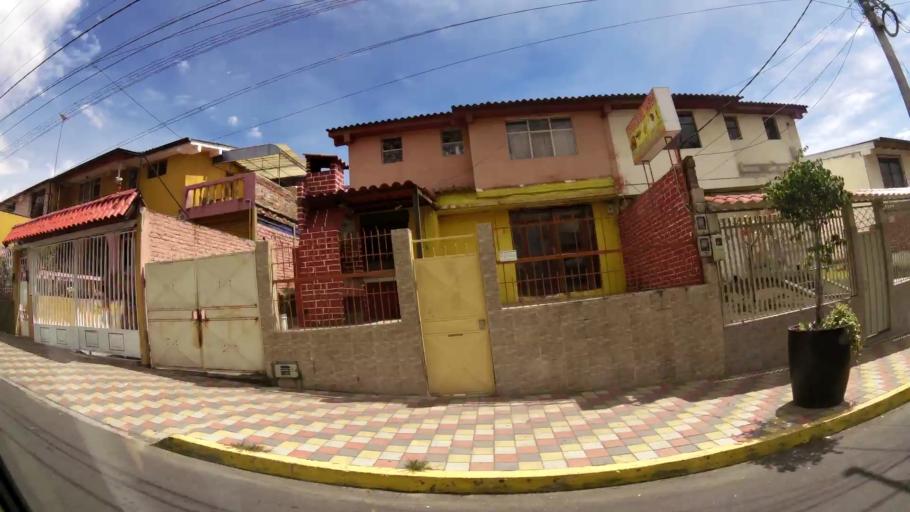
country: EC
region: Tungurahua
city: Ambato
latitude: -1.2610
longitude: -78.6275
